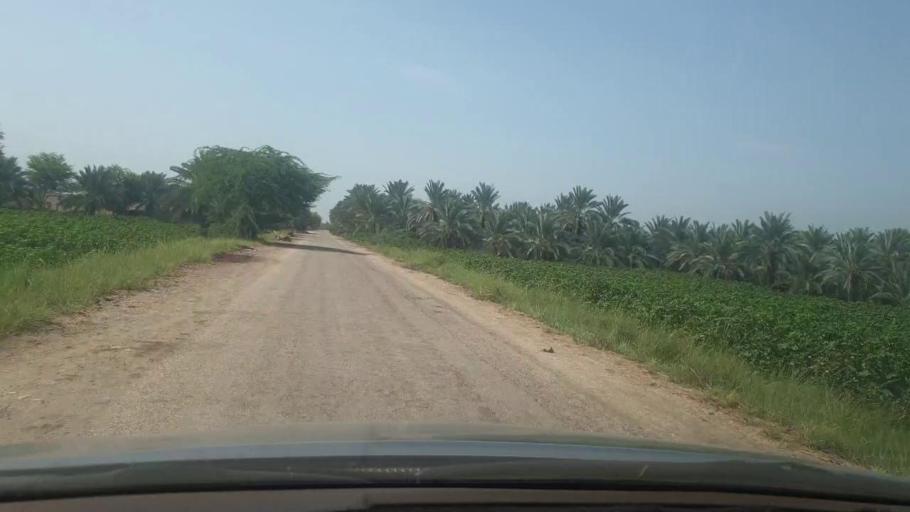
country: PK
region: Sindh
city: Ranipur
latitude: 27.2691
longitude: 68.5817
